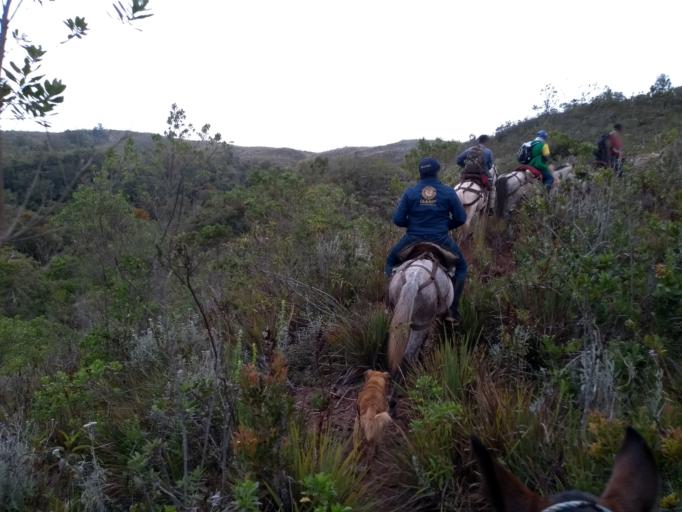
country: CO
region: Cesar
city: Manaure Balcon del Cesar
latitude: 10.2129
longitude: -73.0110
